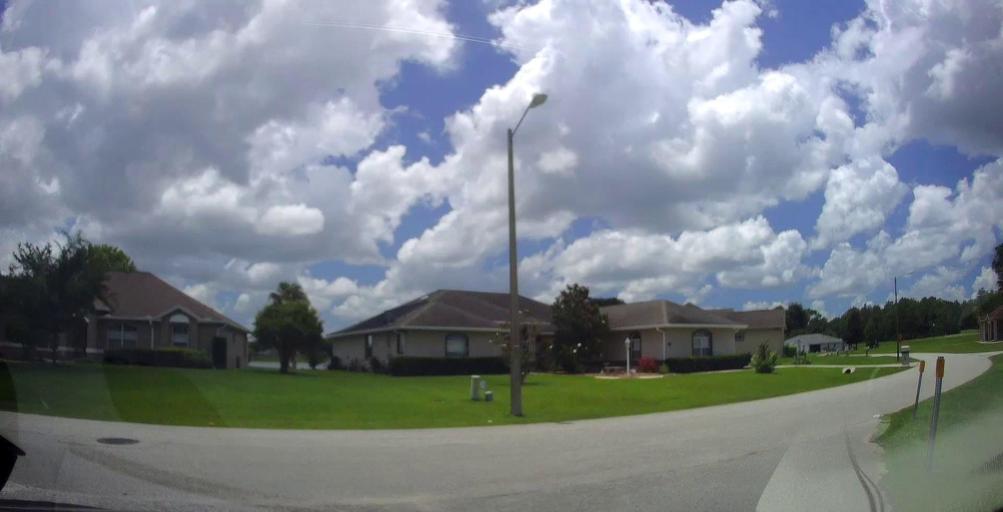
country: US
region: Florida
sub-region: Marion County
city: Silver Springs Shores
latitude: 29.1351
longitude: -82.0117
